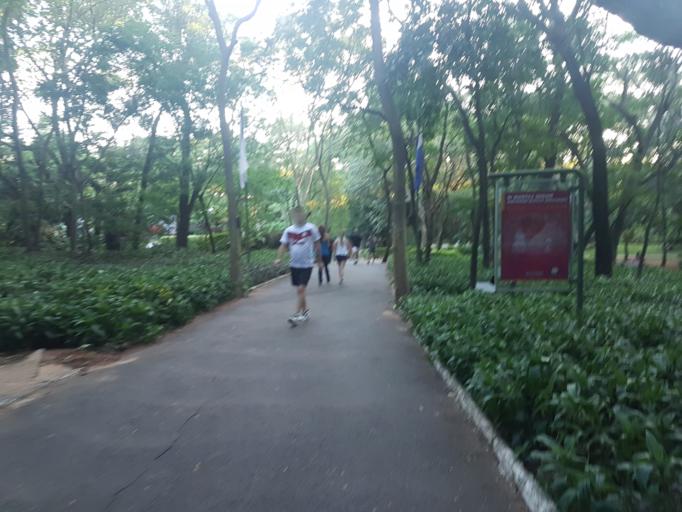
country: PY
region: Asuncion
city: Asuncion
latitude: -25.2755
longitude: -57.5781
